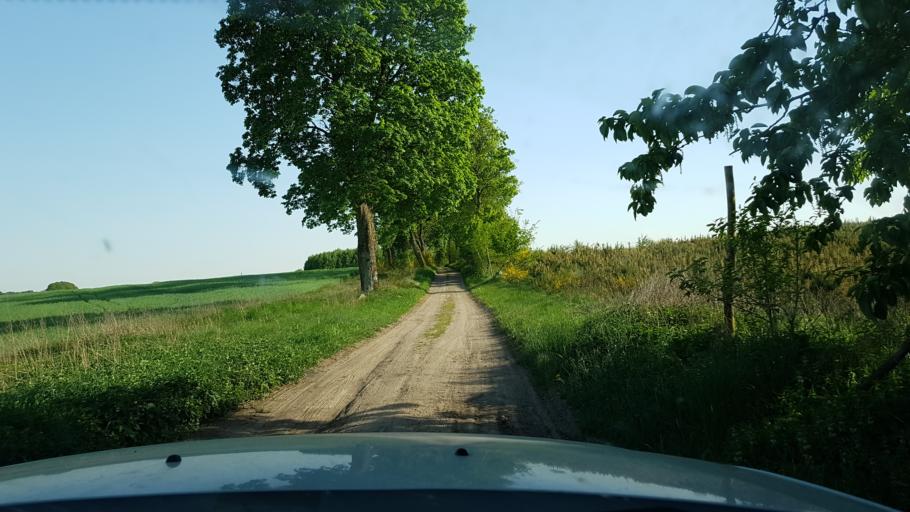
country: PL
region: West Pomeranian Voivodeship
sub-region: Powiat lobeski
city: Resko
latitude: 53.6972
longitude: 15.3361
